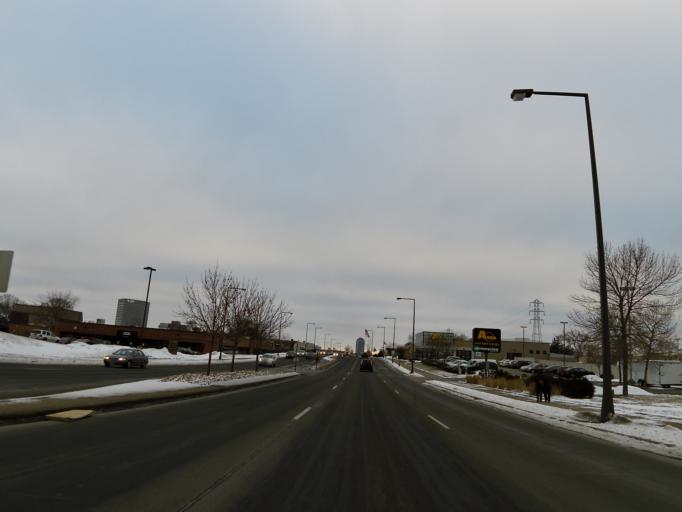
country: US
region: Minnesota
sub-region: Hennepin County
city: Bloomington
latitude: 44.8595
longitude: -93.2910
